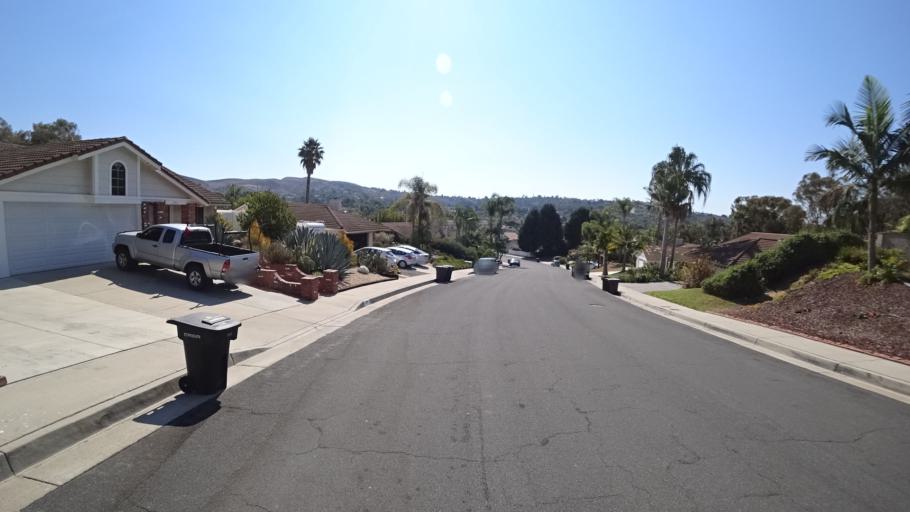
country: US
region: California
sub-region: Orange County
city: San Juan Capistrano
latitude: 33.4734
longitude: -117.6306
